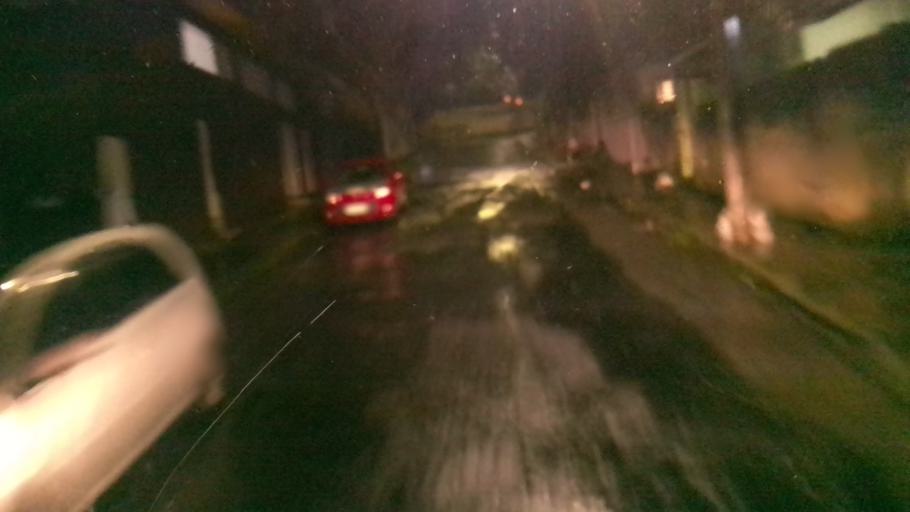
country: BR
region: Minas Gerais
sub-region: Belo Horizonte
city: Belo Horizonte
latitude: -19.8996
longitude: -43.9510
